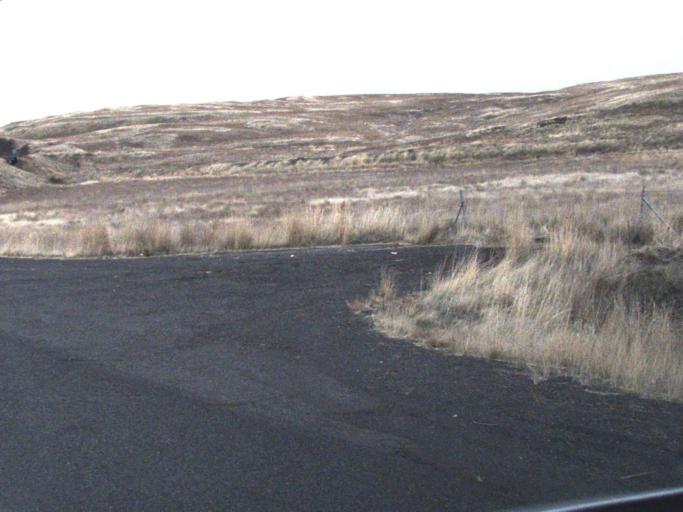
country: US
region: Washington
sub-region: Adams County
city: Ritzville
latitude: 46.7509
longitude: -118.2816
